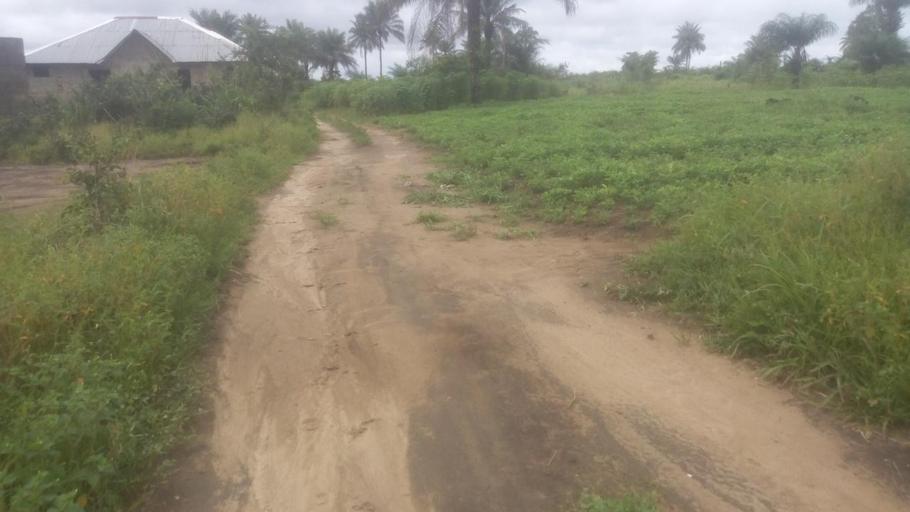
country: SL
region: Northern Province
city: Masoyila
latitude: 8.5905
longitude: -13.1849
